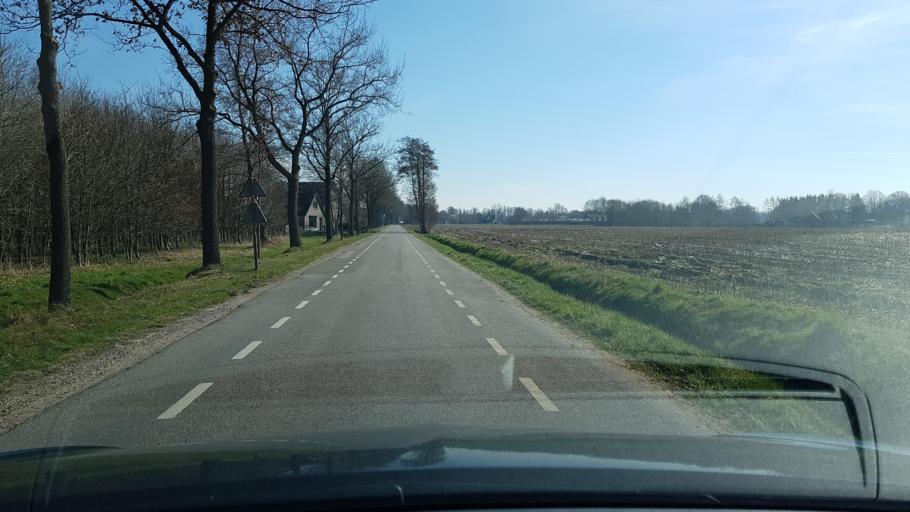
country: NL
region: Gelderland
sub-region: Gemeente Epe
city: Emst
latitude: 52.3074
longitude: 5.9556
